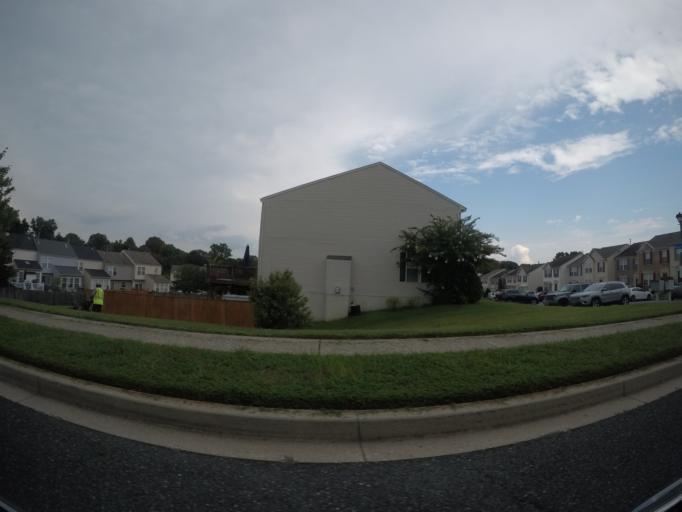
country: US
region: Maryland
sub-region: Harford County
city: Joppatowne
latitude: 39.4734
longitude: -76.3293
